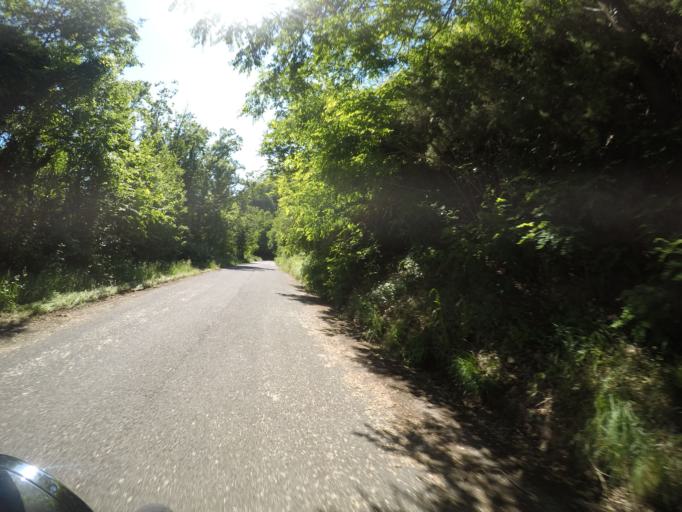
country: IT
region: Tuscany
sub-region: Provincia di Massa-Carrara
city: Fosdinovo
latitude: 44.1459
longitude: 10.0964
